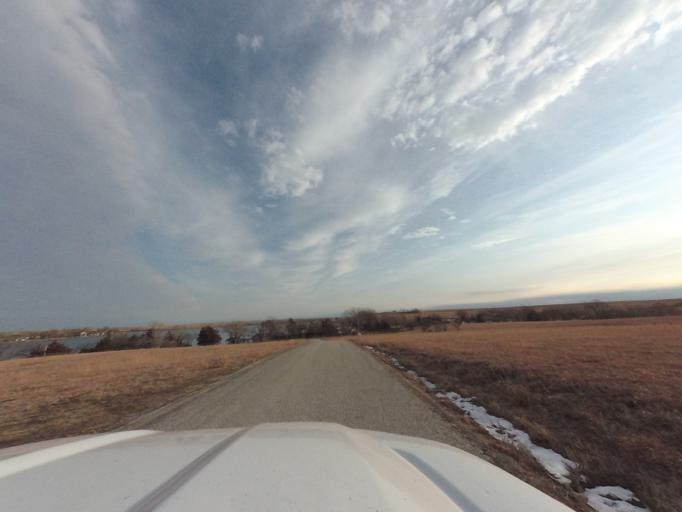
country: US
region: Kansas
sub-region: Morris County
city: Council Grove
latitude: 38.5185
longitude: -96.4205
